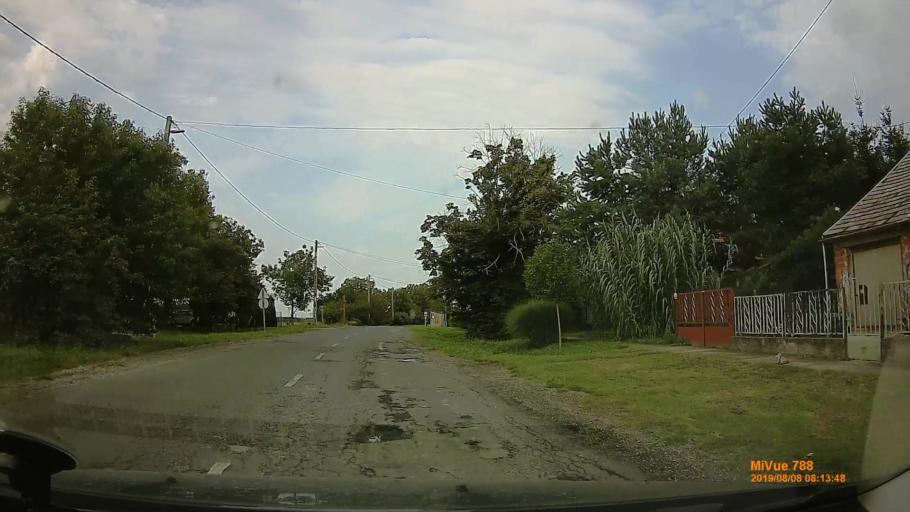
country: HU
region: Zala
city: Murakeresztur
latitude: 46.4021
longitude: 16.8599
